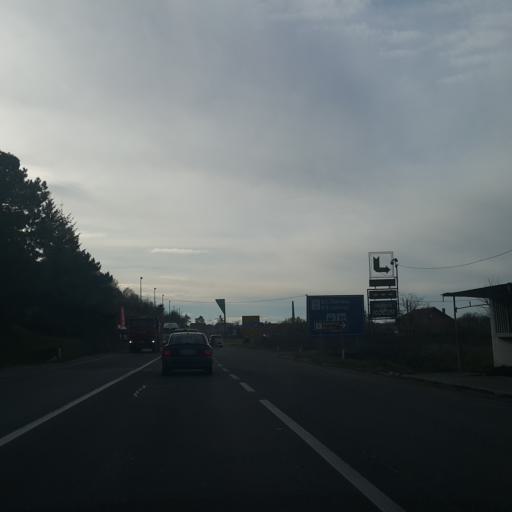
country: RS
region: Central Serbia
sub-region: Kolubarski Okrug
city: Lajkovac
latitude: 44.3663
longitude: 20.2006
